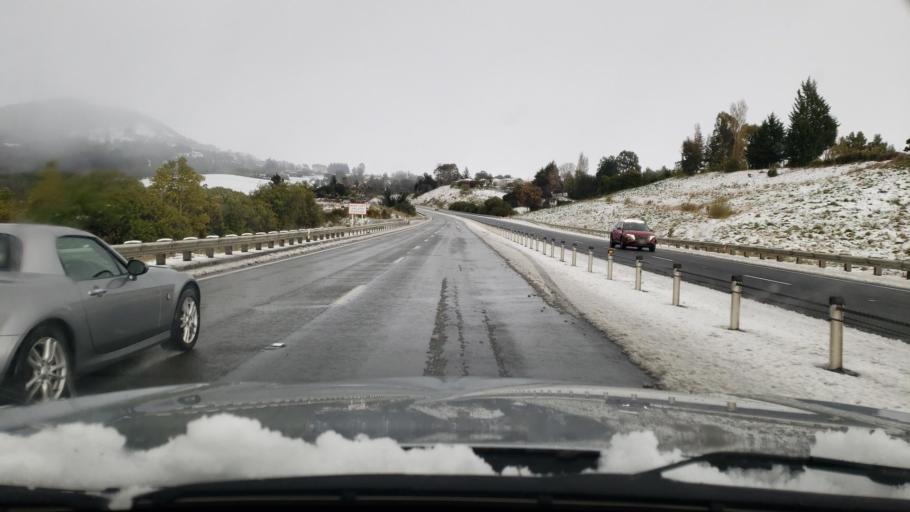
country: NZ
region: Otago
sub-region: Dunedin City
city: Dunedin
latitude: -45.9024
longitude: 170.3931
